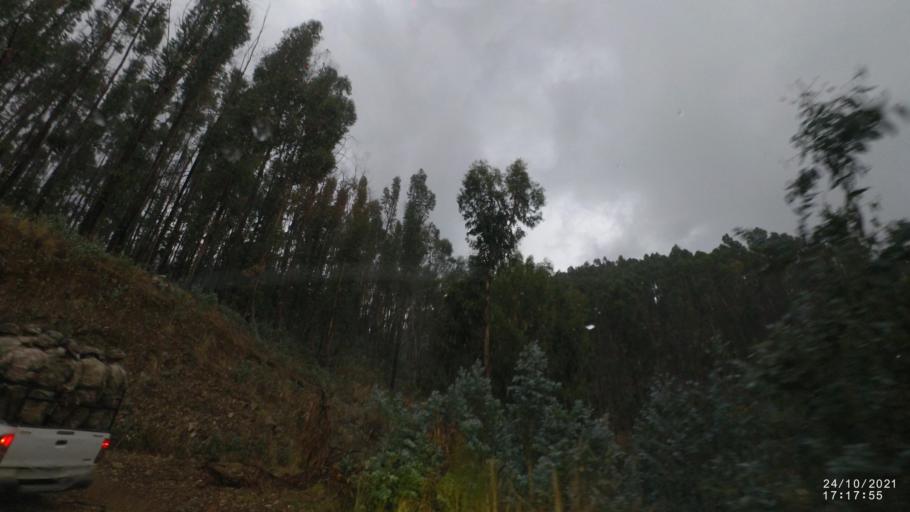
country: BO
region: Cochabamba
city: Cochabamba
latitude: -17.3299
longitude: -66.1361
